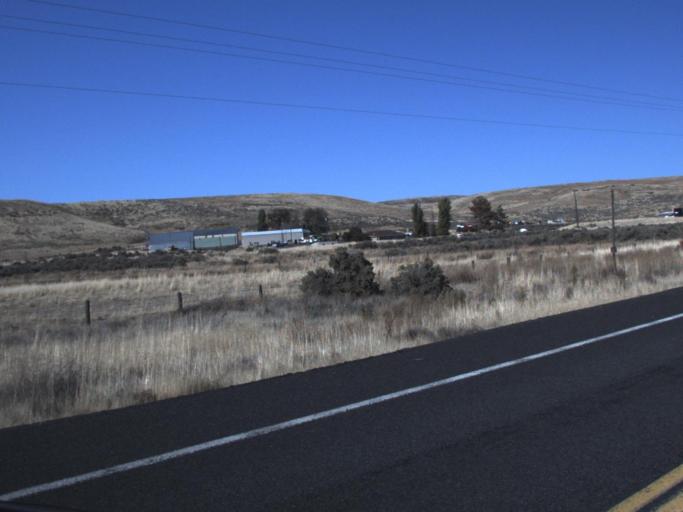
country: US
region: Washington
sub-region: Franklin County
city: Connell
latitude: 46.6608
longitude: -118.4908
